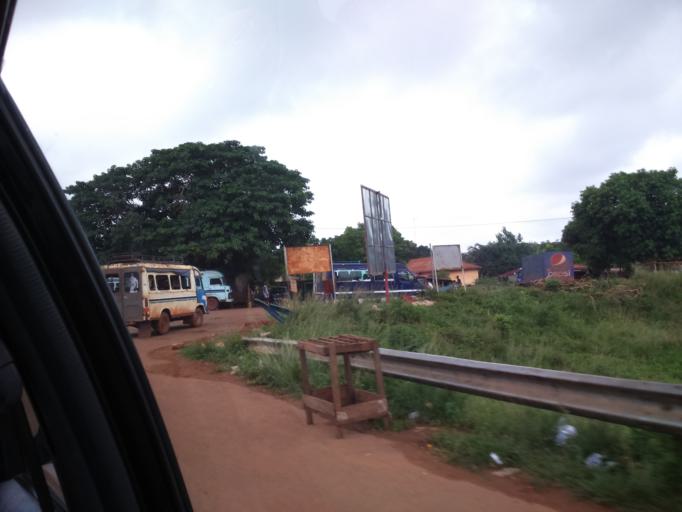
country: CI
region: Moyen-Comoe
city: Abengourou
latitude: 6.7234
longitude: -3.4869
